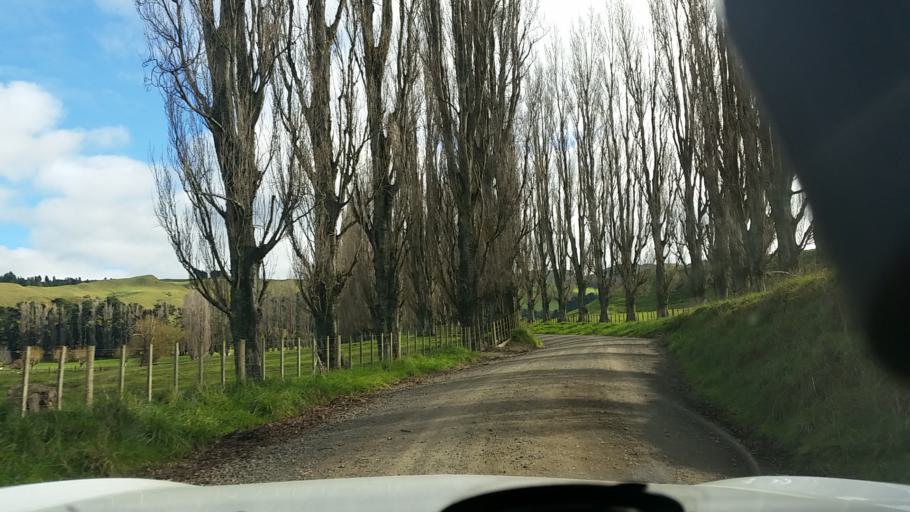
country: NZ
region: Hawke's Bay
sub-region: Napier City
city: Napier
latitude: -39.1018
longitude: 176.8804
